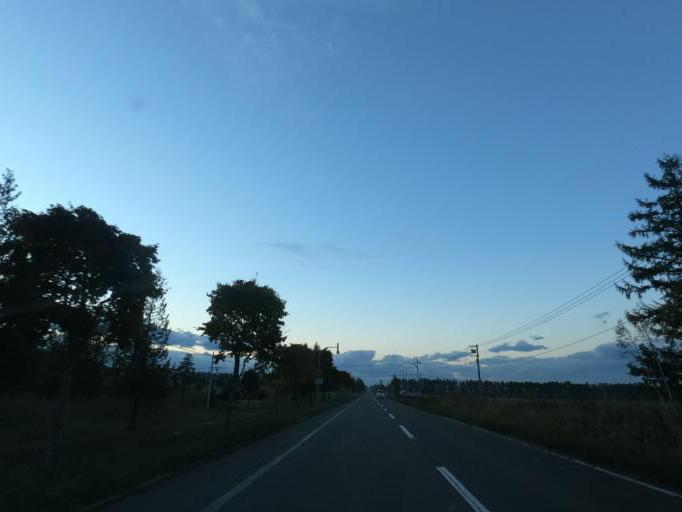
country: JP
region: Hokkaido
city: Obihiro
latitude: 42.6410
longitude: 143.2032
